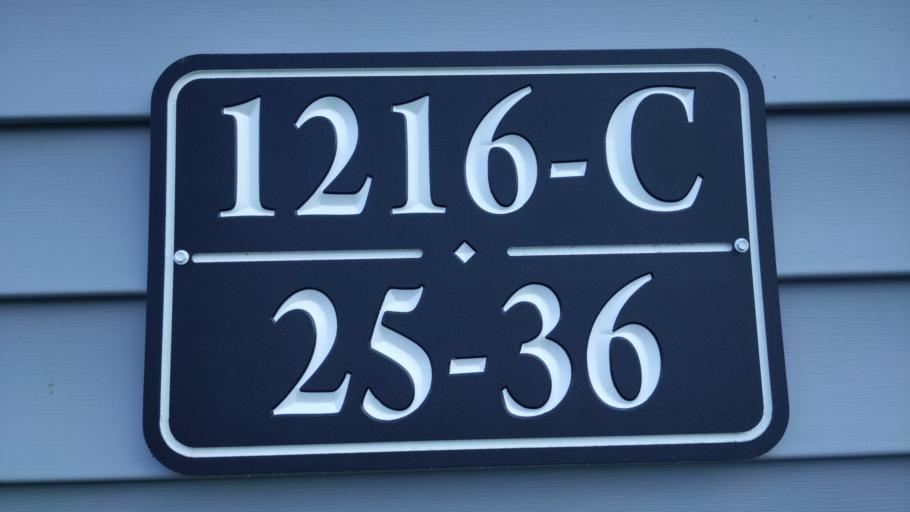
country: US
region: Virginia
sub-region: Montgomery County
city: Blacksburg
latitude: 37.2415
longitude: -80.4337
